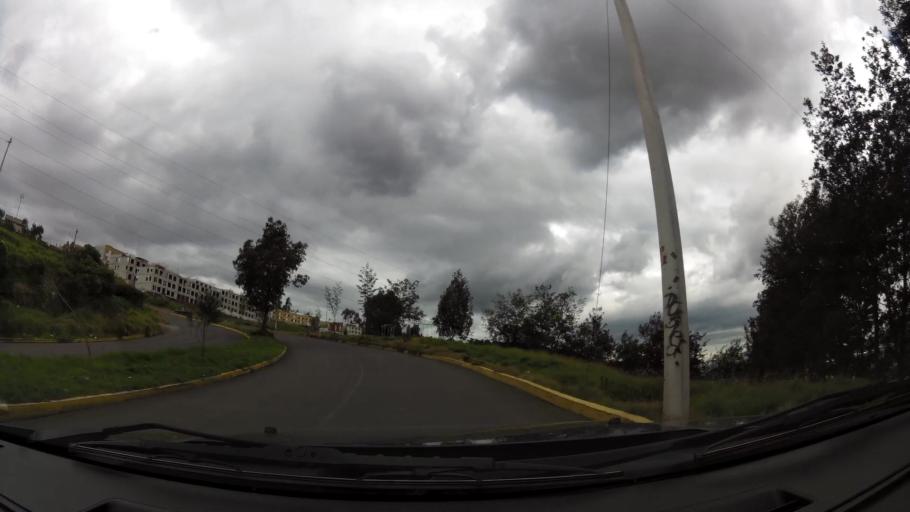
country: EC
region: Pichincha
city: Sangolqui
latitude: -0.3295
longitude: -78.5270
